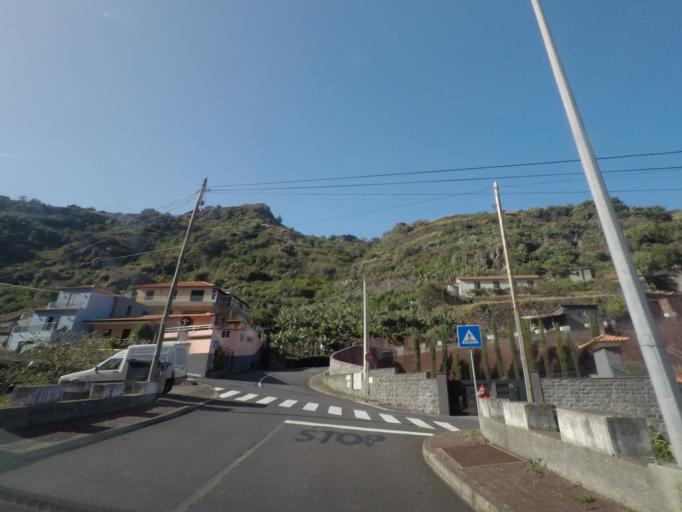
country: PT
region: Madeira
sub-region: Santa Cruz
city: Santa Cruz
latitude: 32.6925
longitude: -16.8010
